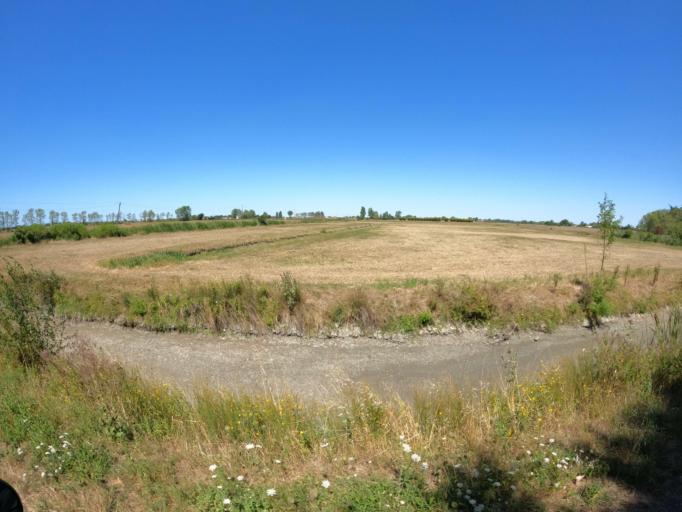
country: FR
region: Pays de la Loire
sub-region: Departement de la Vendee
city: Saint-Jean-de-Monts
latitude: 46.8012
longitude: -2.0765
